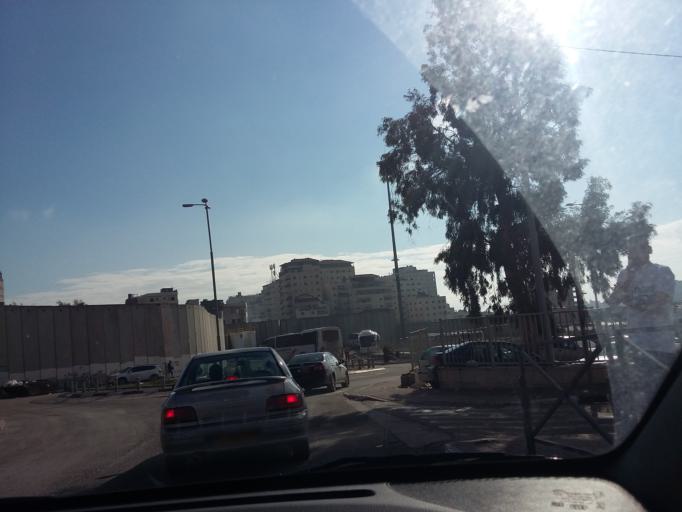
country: PS
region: West Bank
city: `Anata
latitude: 31.8101
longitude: 35.2413
